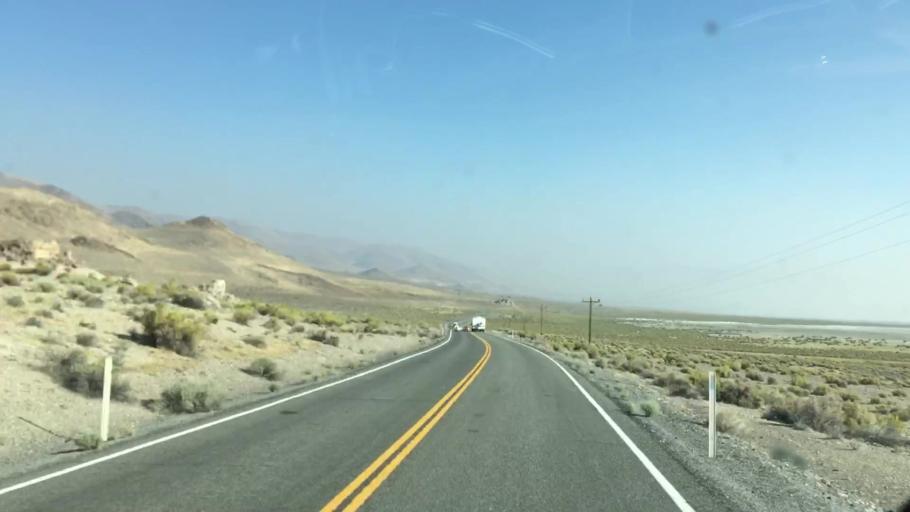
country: US
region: Nevada
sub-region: Lyon County
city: Fernley
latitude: 40.1786
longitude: -119.3684
